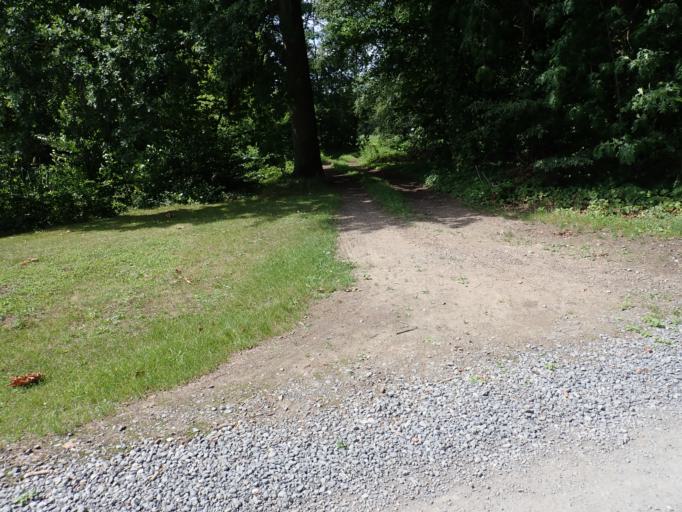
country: BE
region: Flanders
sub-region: Provincie Antwerpen
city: Zandhoven
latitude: 51.2022
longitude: 4.6300
